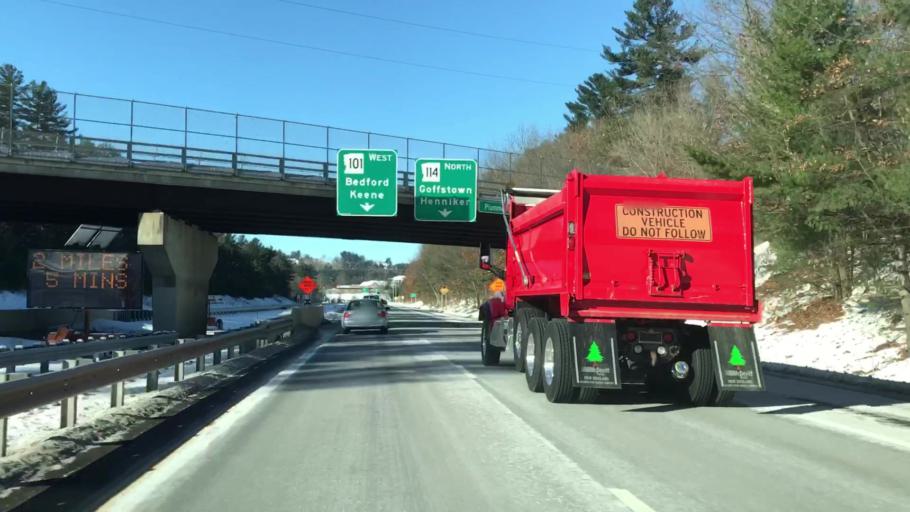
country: US
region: New Hampshire
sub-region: Hillsborough County
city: Bedford
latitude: 42.9584
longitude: -71.4935
